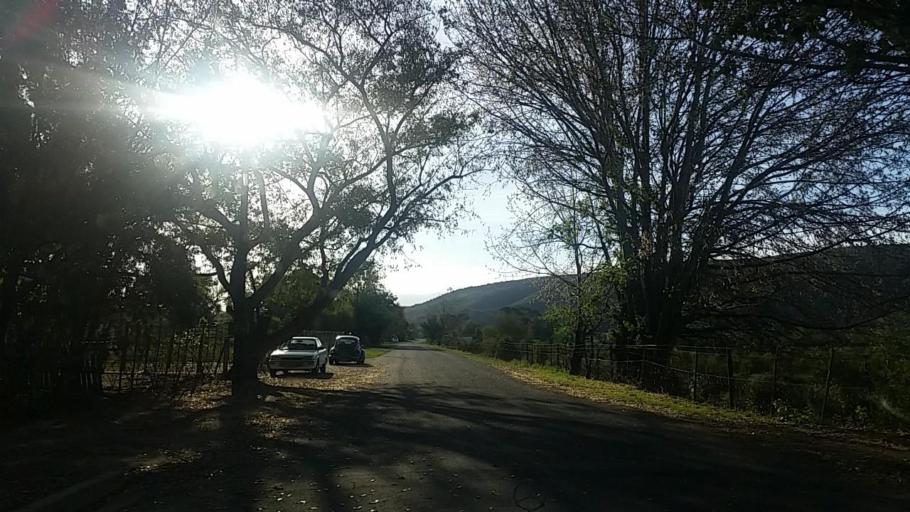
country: ZA
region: Western Cape
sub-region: Eden District Municipality
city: Knysna
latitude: -33.6547
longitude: 23.1347
